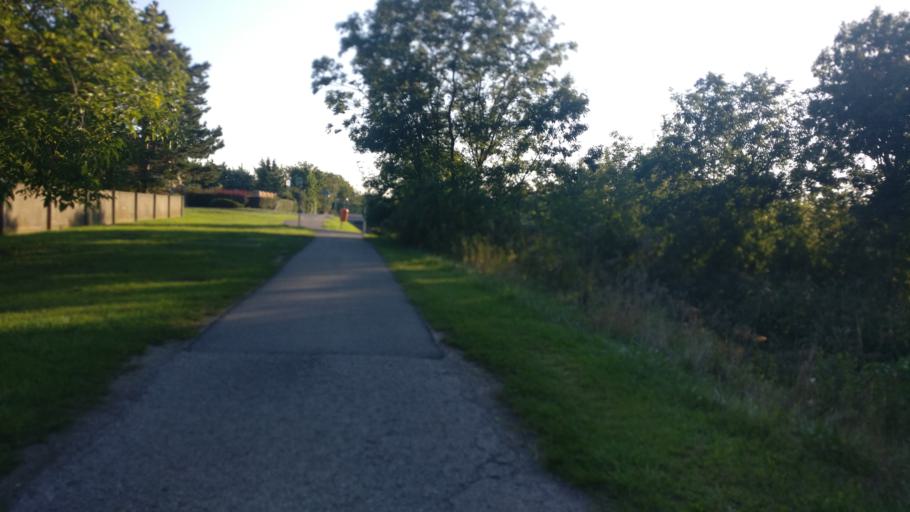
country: AT
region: Lower Austria
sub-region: Politischer Bezirk Wien-Umgebung
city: Himberg
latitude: 48.0879
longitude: 16.4336
